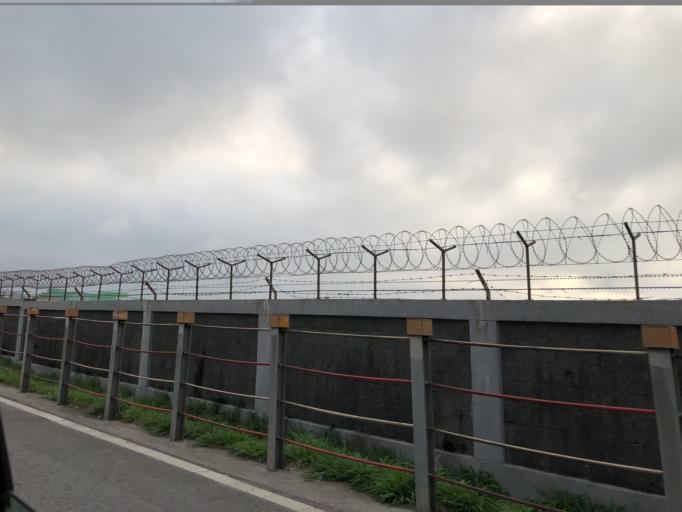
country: TW
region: Taiwan
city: Taoyuan City
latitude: 25.1014
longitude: 121.2486
